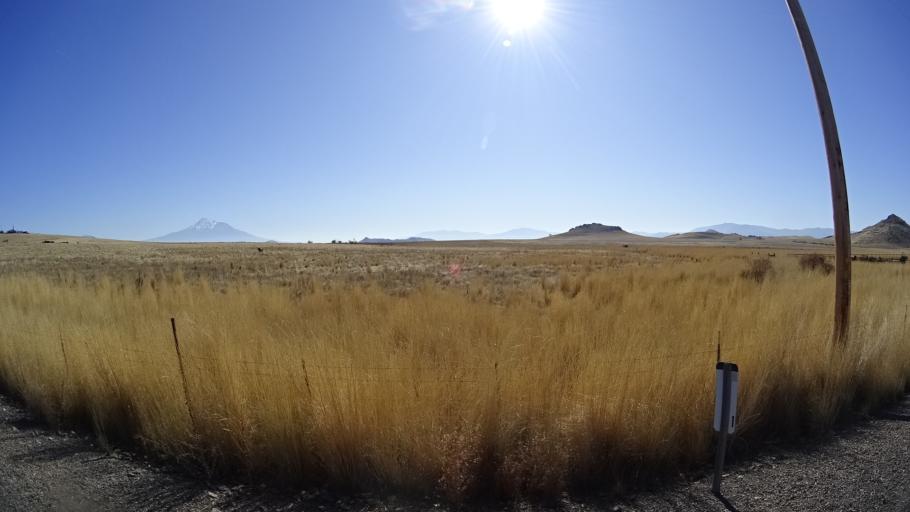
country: US
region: California
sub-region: Siskiyou County
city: Montague
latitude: 41.7559
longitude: -122.4758
